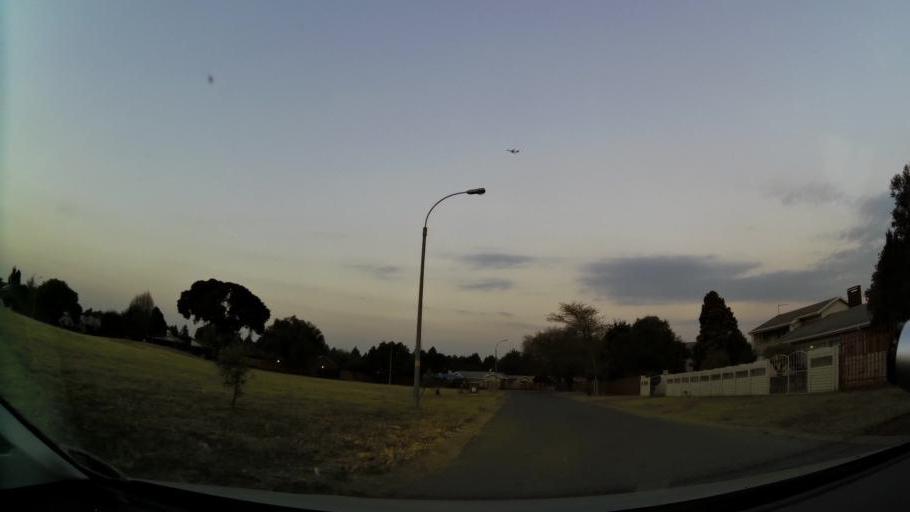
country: ZA
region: Gauteng
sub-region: Ekurhuleni Metropolitan Municipality
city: Tembisa
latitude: -26.0512
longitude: 28.2434
